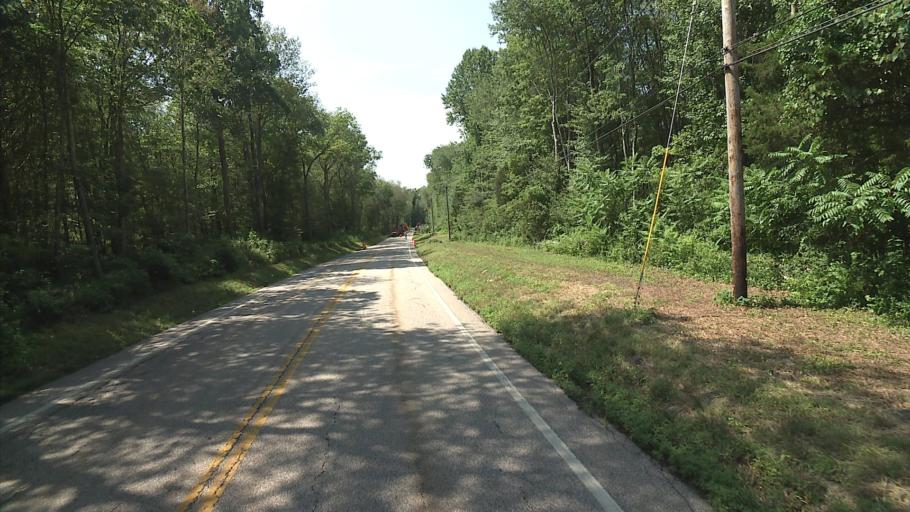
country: US
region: Connecticut
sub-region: New London County
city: Montville Center
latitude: 41.4180
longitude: -72.2150
